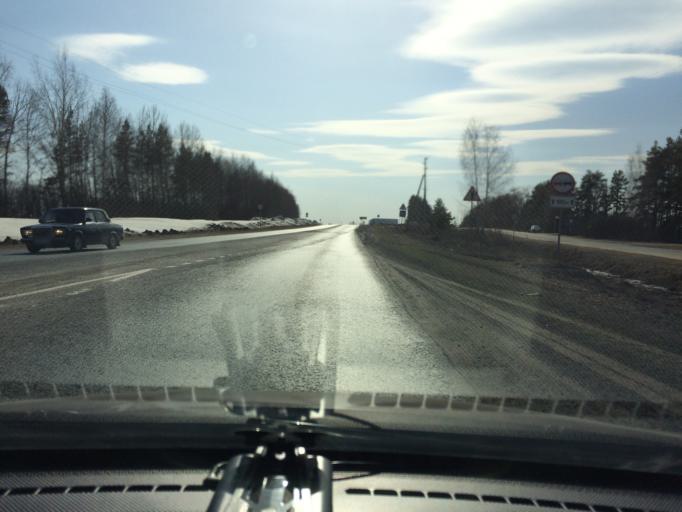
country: RU
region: Mariy-El
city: Yoshkar-Ola
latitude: 56.7203
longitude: 48.1050
